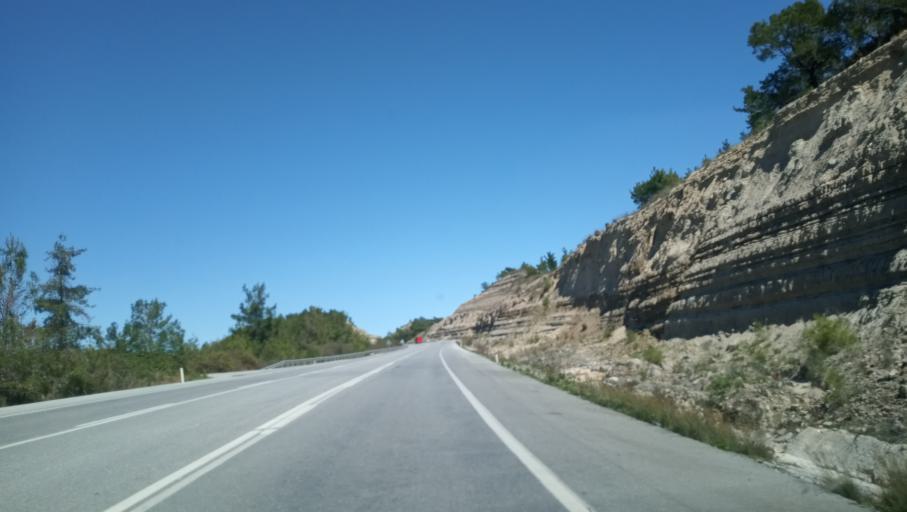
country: TR
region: Antalya
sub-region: Manavgat
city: Kizilagac
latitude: 36.7421
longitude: 31.6156
